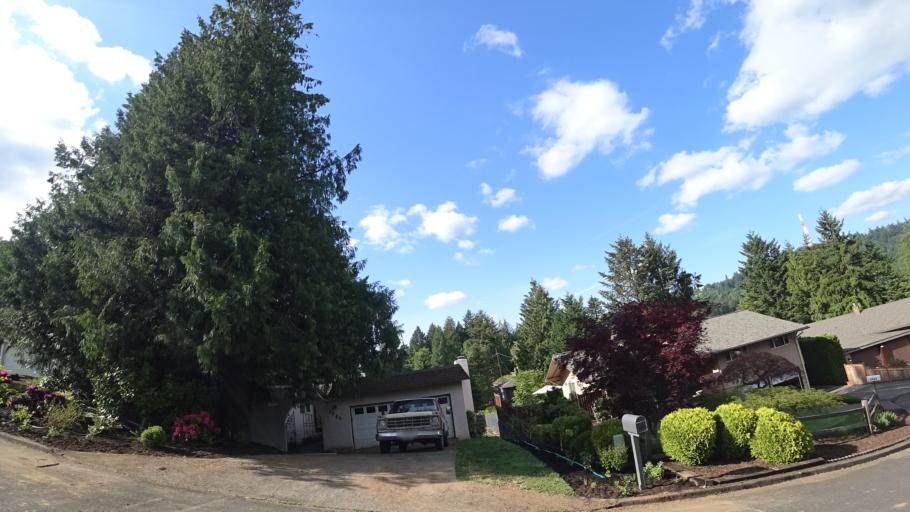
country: US
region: Oregon
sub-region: Washington County
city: Garden Home-Whitford
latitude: 45.4803
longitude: -122.7138
